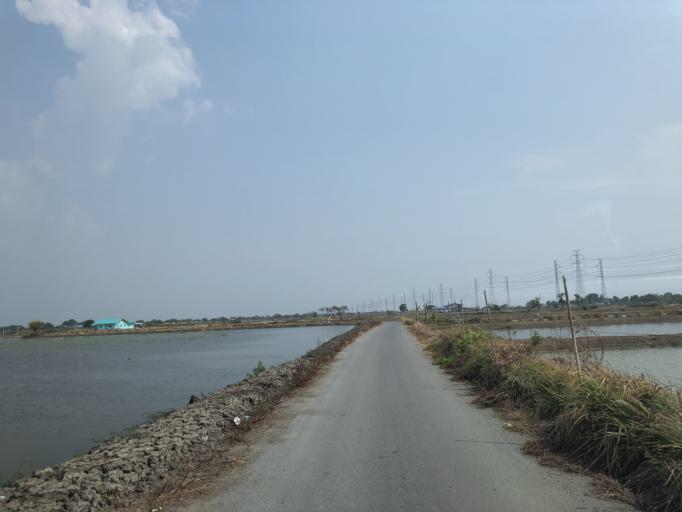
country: TH
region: Samut Prakan
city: Bang Bo
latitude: 13.5468
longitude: 100.8820
